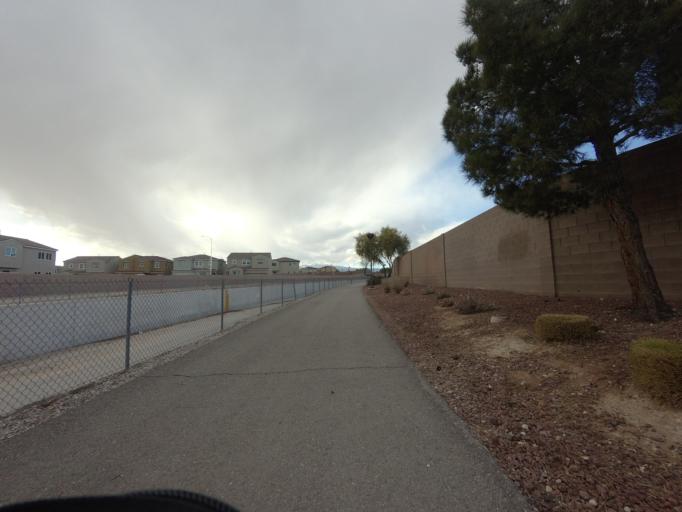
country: US
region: Nevada
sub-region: Clark County
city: North Las Vegas
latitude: 36.2637
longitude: -115.1910
